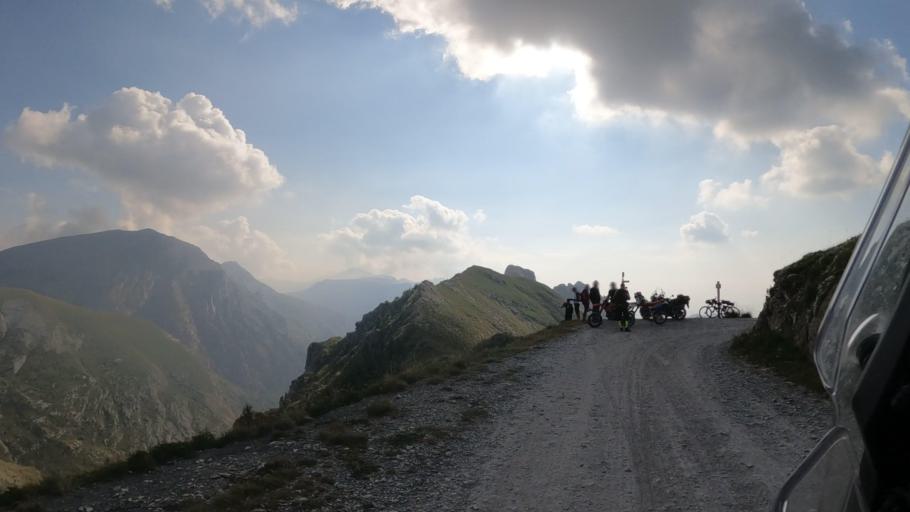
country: IT
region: Piedmont
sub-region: Provincia di Cuneo
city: Briga Alta
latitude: 44.1473
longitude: 7.6950
